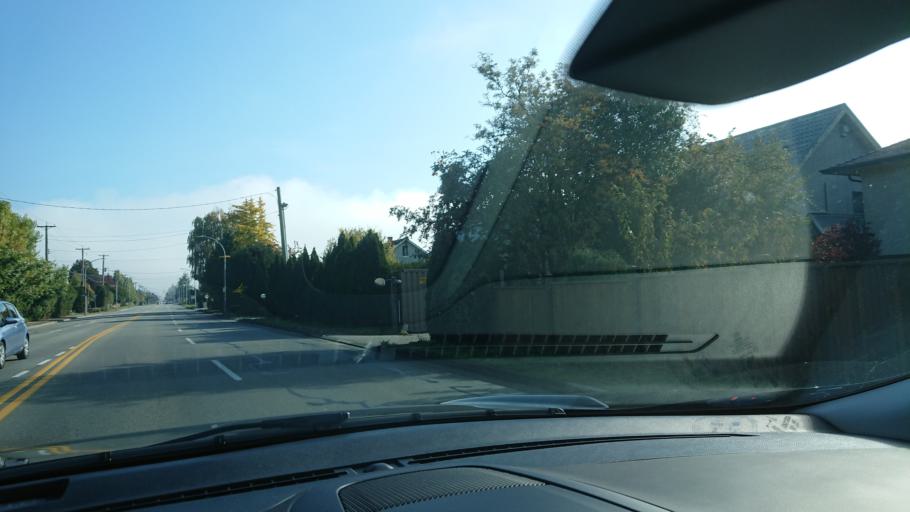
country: CA
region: British Columbia
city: Richmond
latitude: 49.1335
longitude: -123.1569
